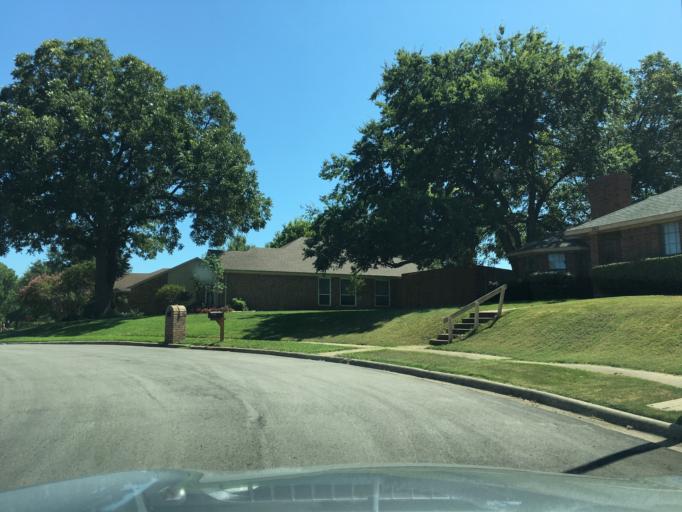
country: US
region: Texas
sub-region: Dallas County
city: Garland
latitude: 32.9525
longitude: -96.6290
